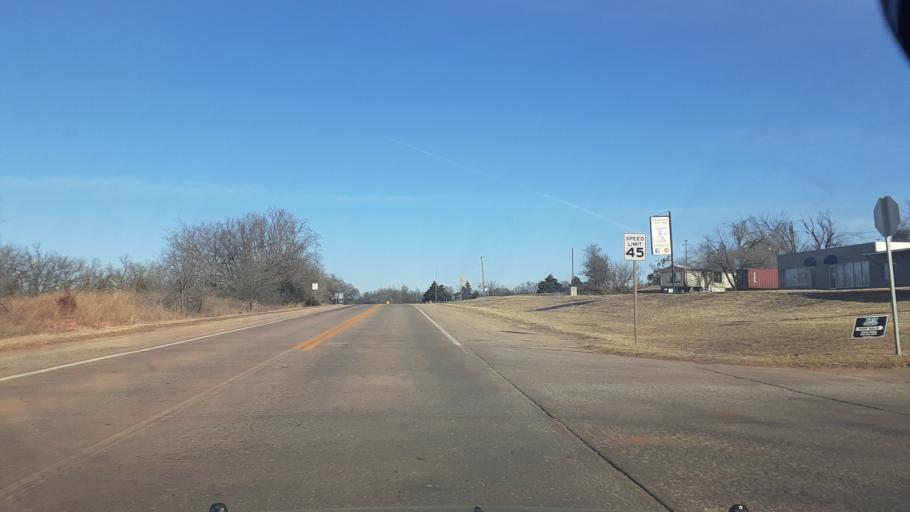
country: US
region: Oklahoma
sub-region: Logan County
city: Guthrie
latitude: 35.8909
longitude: -97.4240
